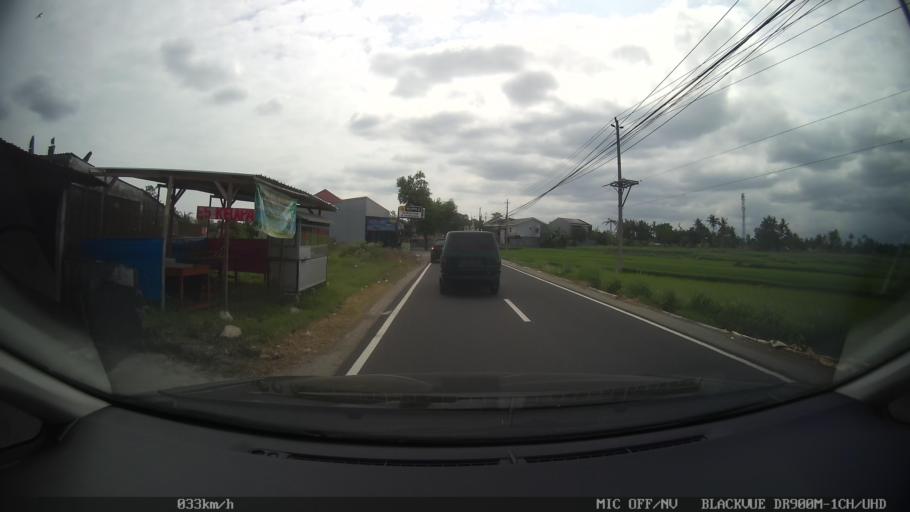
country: ID
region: Daerah Istimewa Yogyakarta
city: Depok
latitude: -7.7310
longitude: 110.4547
